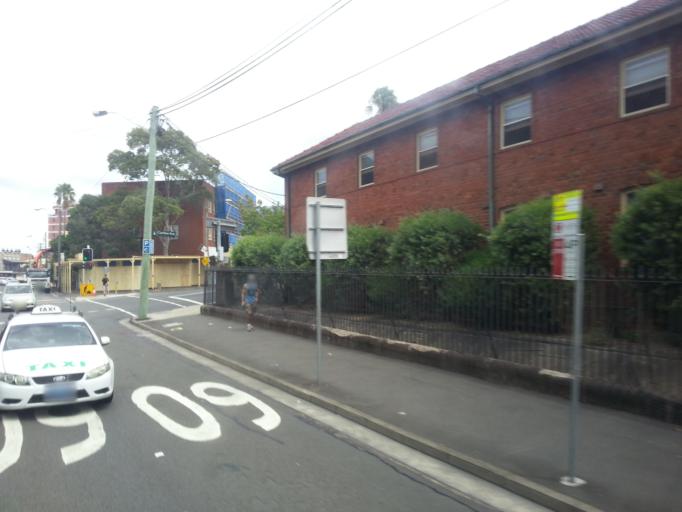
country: AU
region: New South Wales
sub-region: City of Sydney
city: Darlington
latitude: -33.8911
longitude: 151.1885
